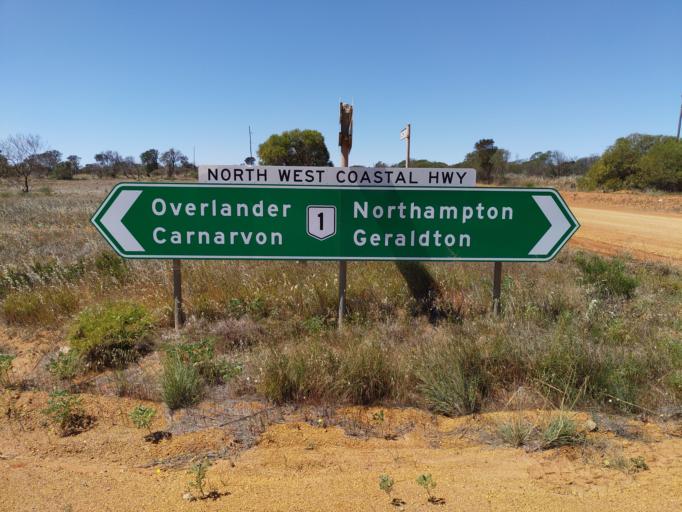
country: AU
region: Western Australia
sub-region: Northampton Shire
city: Northampton
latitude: -27.9409
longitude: 114.6867
